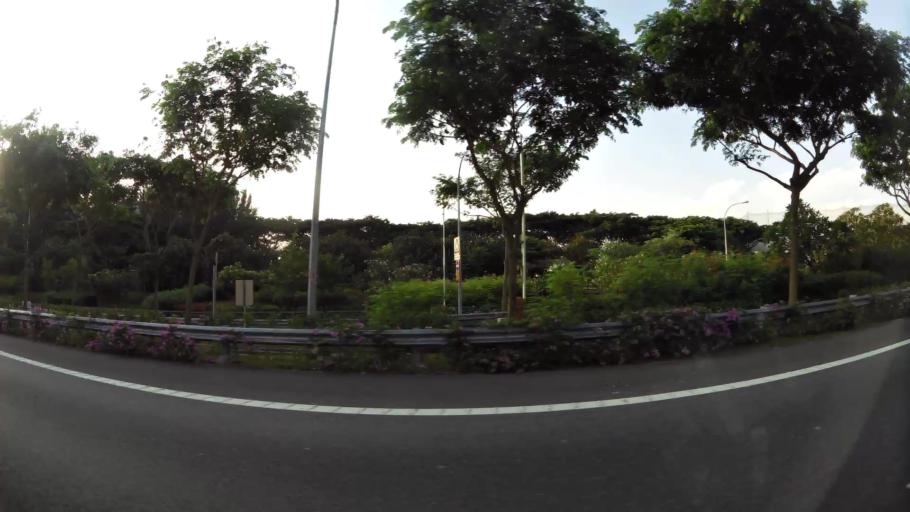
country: SG
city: Singapore
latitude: 1.2953
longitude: 103.8749
